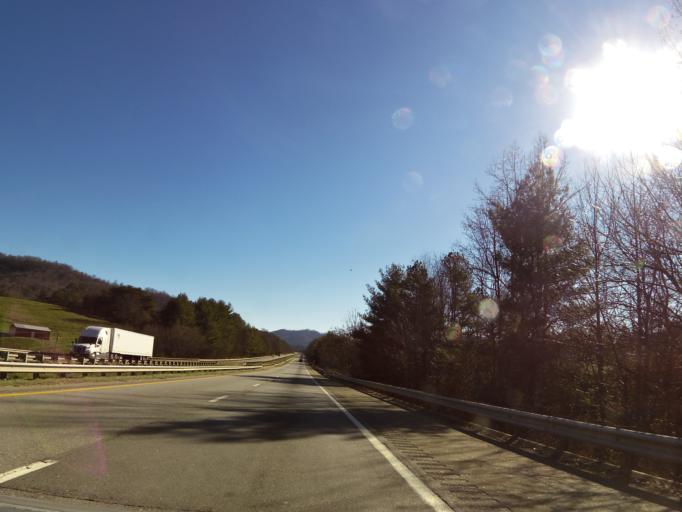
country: US
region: North Carolina
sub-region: Haywood County
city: Lake Junaluska
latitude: 35.5509
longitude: -82.9402
